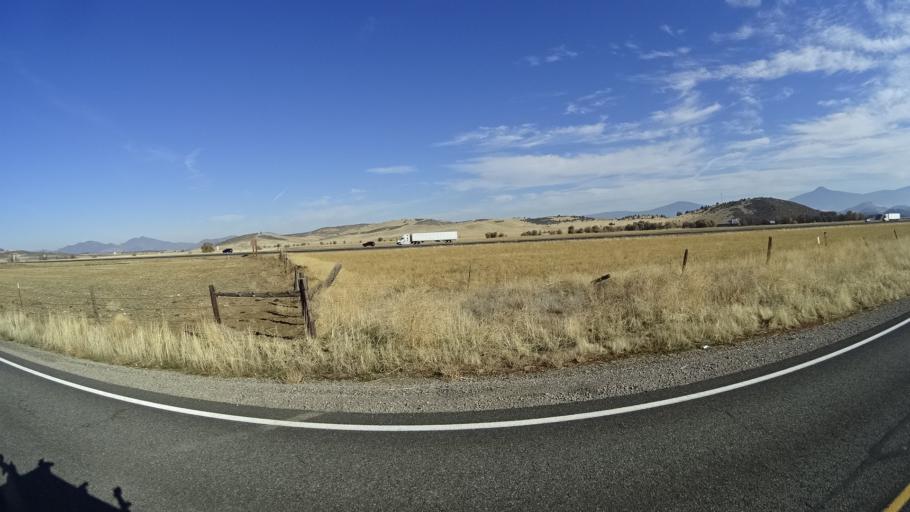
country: US
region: California
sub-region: Siskiyou County
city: Montague
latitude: 41.6480
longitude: -122.5457
